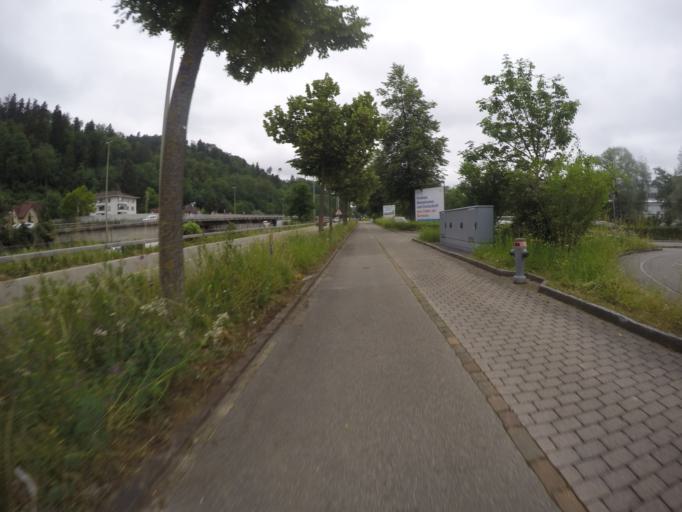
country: CH
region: Zurich
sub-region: Bezirk Winterthur
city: Toess (Kreis 4) / Eichliacker
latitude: 47.4864
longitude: 8.7030
